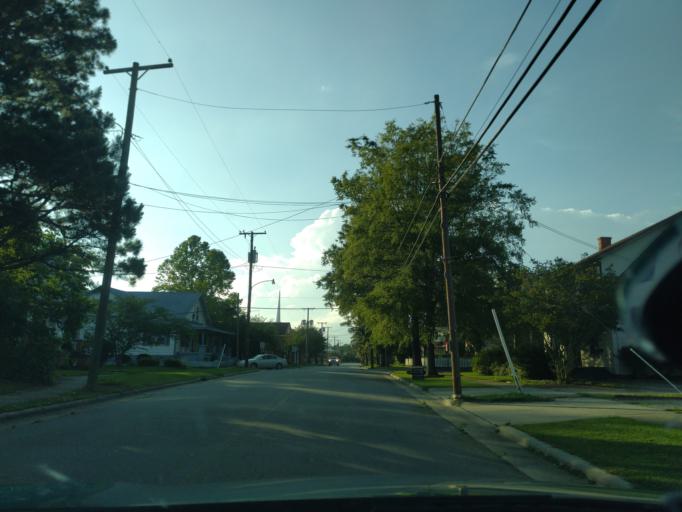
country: US
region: North Carolina
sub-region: Washington County
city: Plymouth
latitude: 35.8634
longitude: -76.7485
